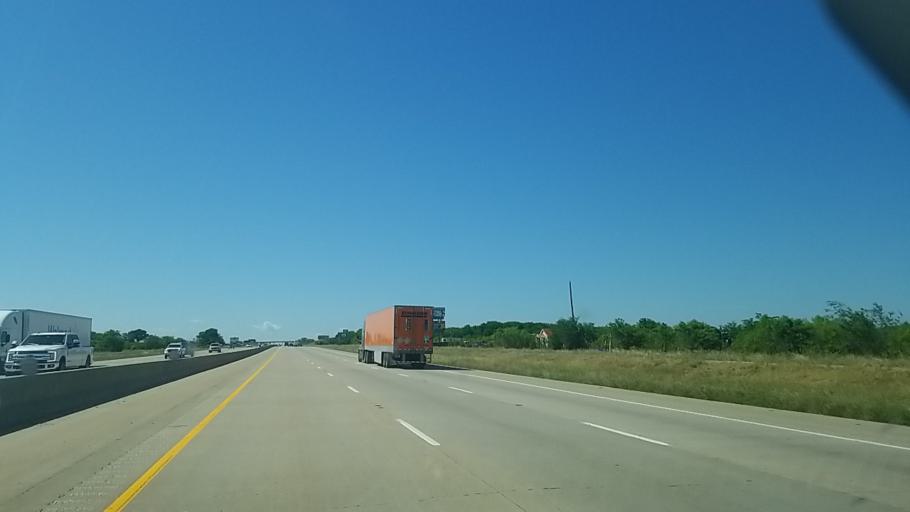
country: US
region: Texas
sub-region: Navarro County
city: Corsicana
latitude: 32.2062
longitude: -96.4771
